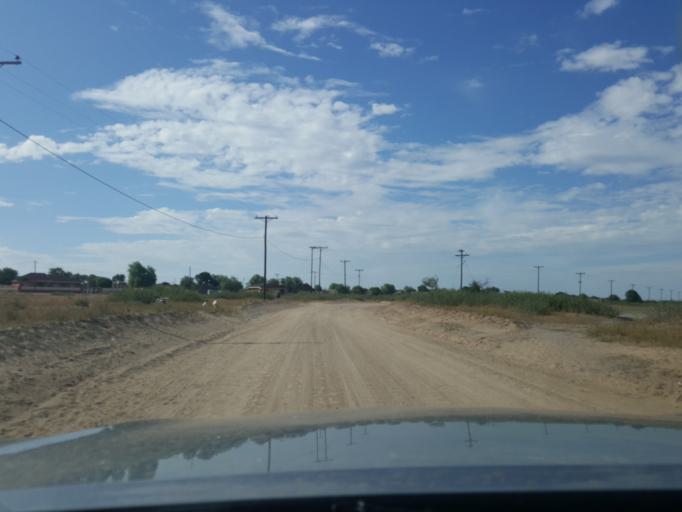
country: BW
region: Kweneng
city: Khudumelapye
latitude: -23.6931
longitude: 24.7170
